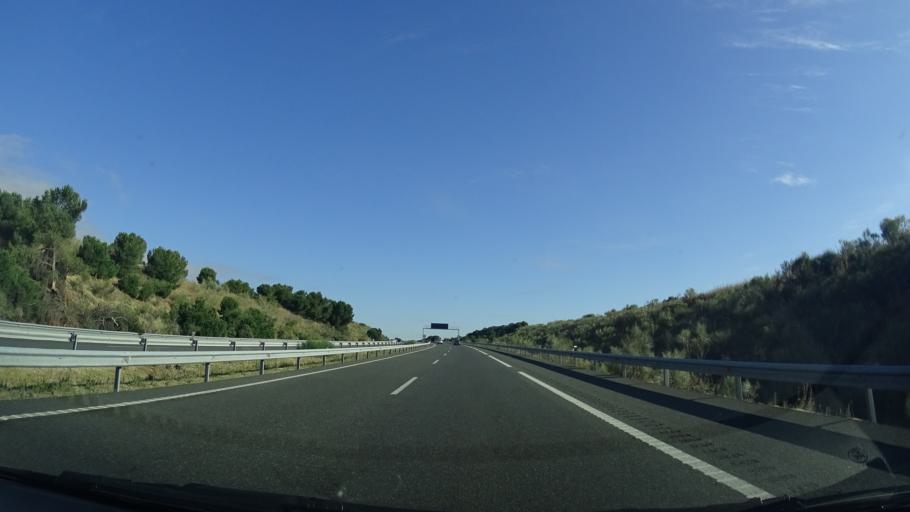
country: ES
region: Castille and Leon
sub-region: Provincia de Avila
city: Sanchidrian
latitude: 40.8733
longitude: -4.5670
